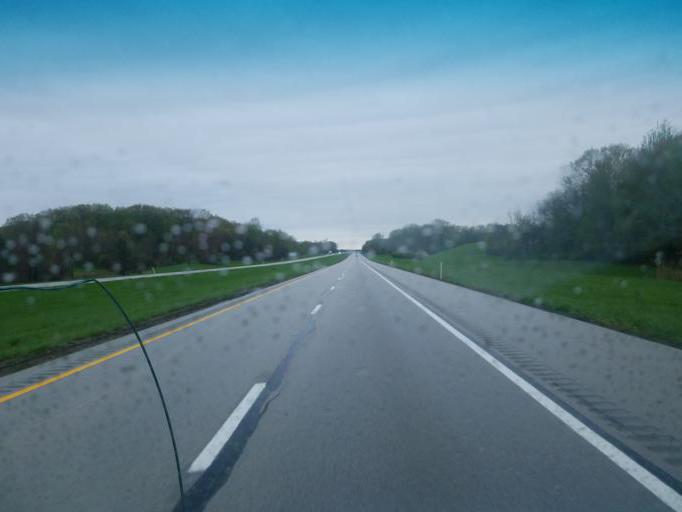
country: US
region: Ohio
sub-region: Ashtabula County
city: North Kingsville
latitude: 41.8662
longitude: -80.6842
